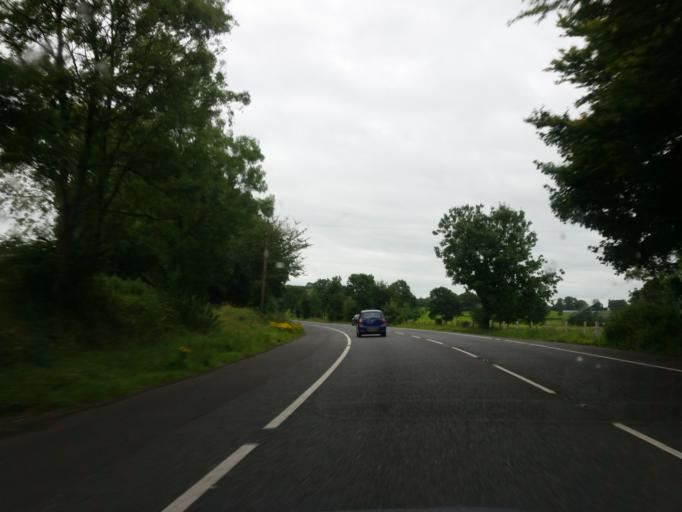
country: GB
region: Northern Ireland
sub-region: Fermanagh District
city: Enniskillen
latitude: 54.3191
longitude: -7.5905
